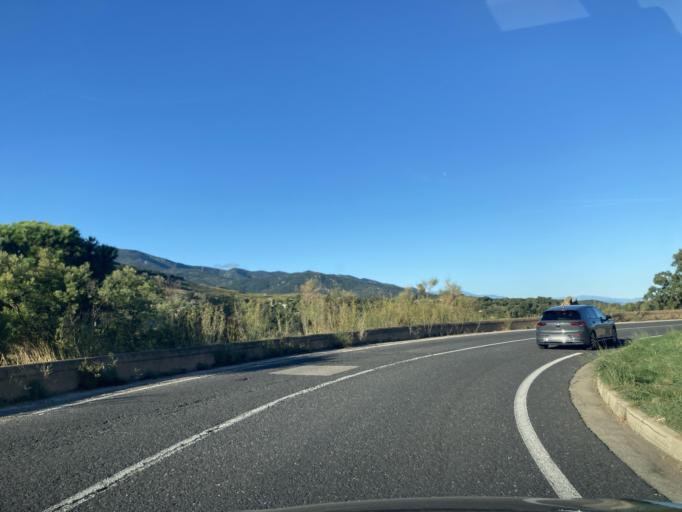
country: FR
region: Languedoc-Roussillon
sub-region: Departement des Pyrenees-Orientales
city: Collioure
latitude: 42.5245
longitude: 3.0743
